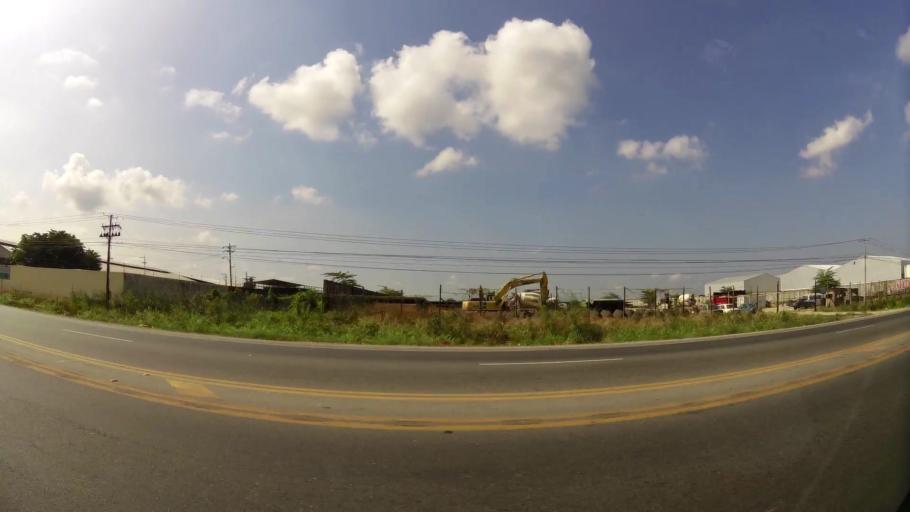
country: EC
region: Guayas
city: Eloy Alfaro
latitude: -2.1783
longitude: -79.8034
